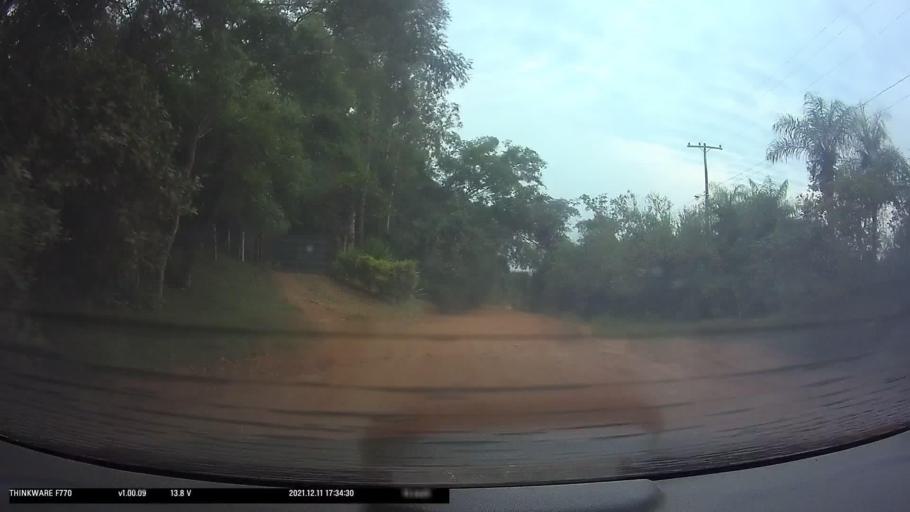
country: PY
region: Cordillera
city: Altos
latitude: -25.3066
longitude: -57.2484
